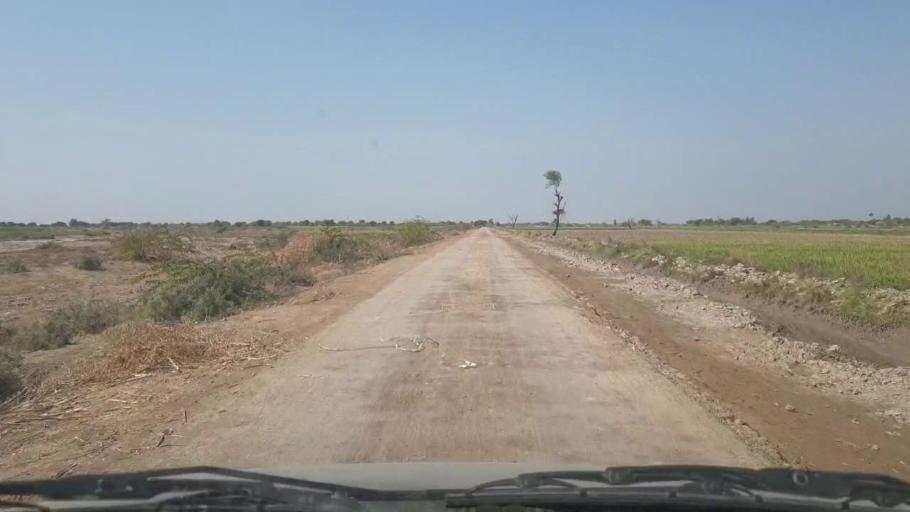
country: PK
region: Sindh
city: Samaro
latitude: 25.2229
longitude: 69.3317
